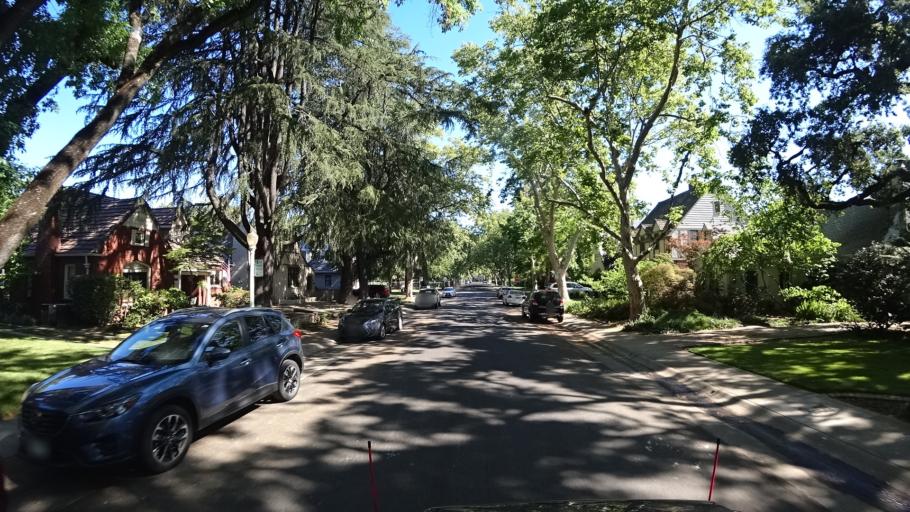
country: US
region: California
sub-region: Sacramento County
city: Sacramento
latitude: 38.5519
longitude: -121.4817
